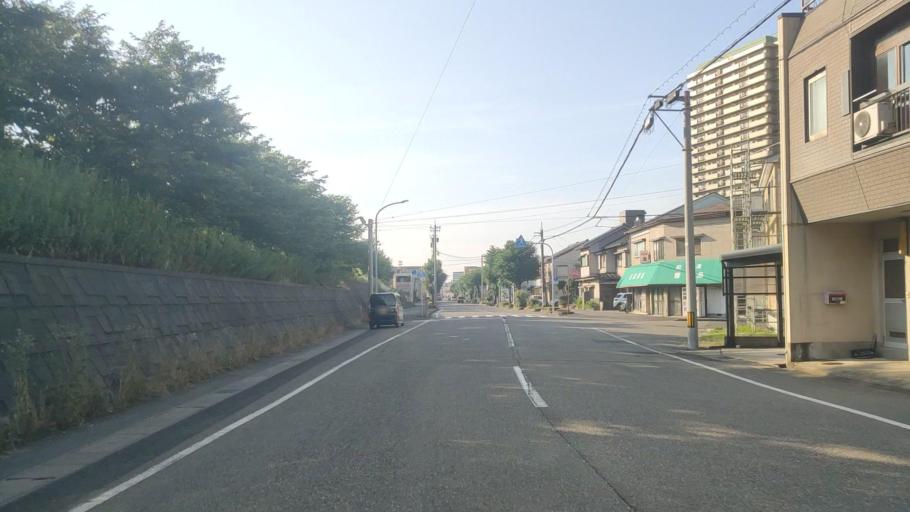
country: JP
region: Fukui
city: Fukui-shi
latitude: 36.0525
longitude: 136.2317
